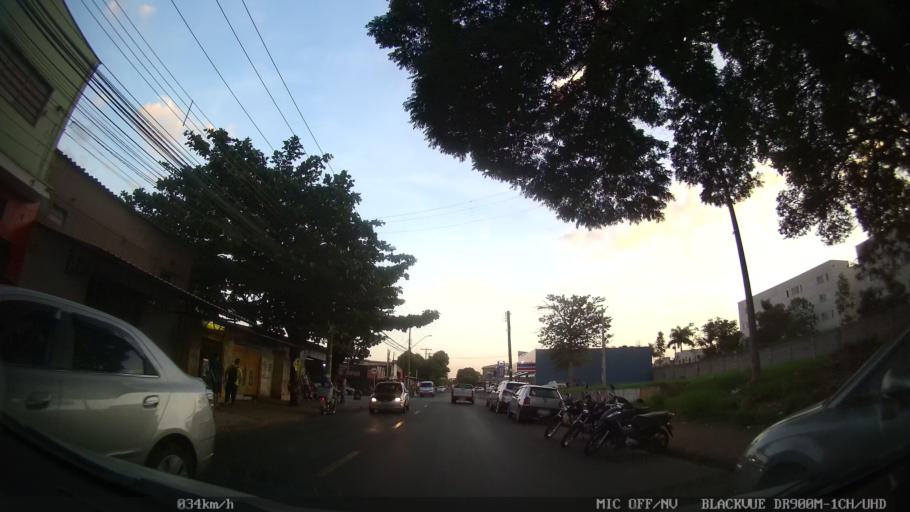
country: BR
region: Sao Paulo
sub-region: Ribeirao Preto
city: Ribeirao Preto
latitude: -21.1302
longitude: -47.8132
